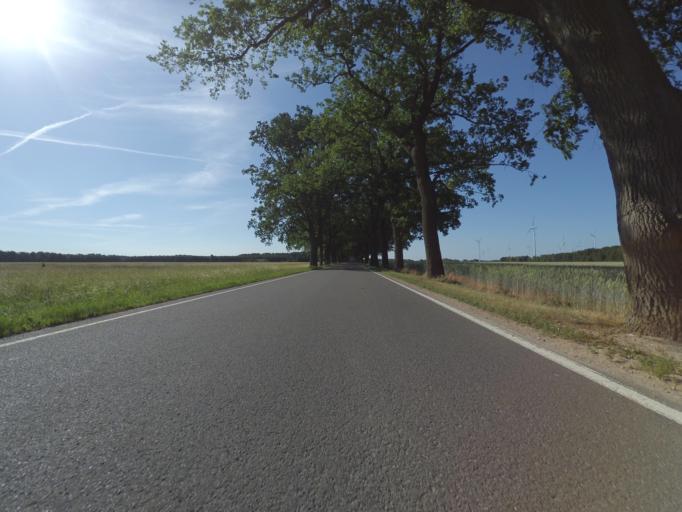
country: DE
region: Brandenburg
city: Putlitz
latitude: 53.3485
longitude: 12.0376
